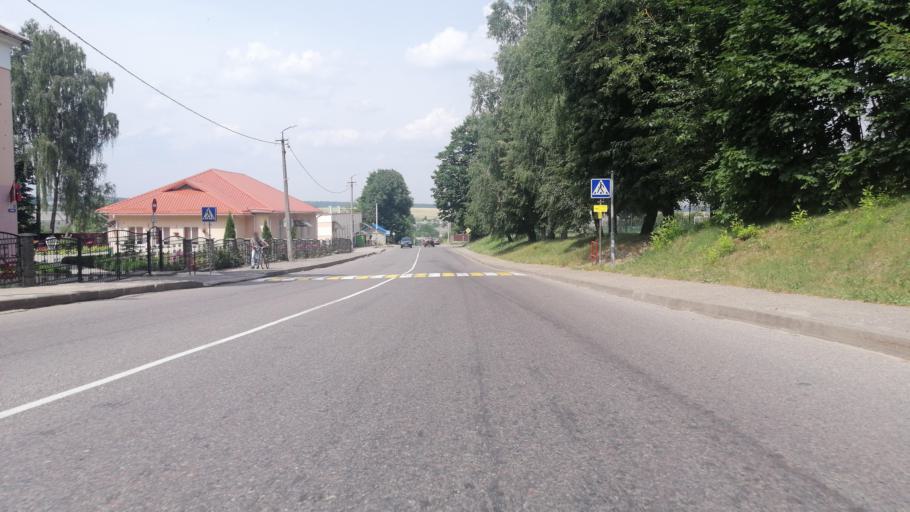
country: BY
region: Grodnenskaya
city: Navahrudak
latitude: 53.6029
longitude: 25.8241
